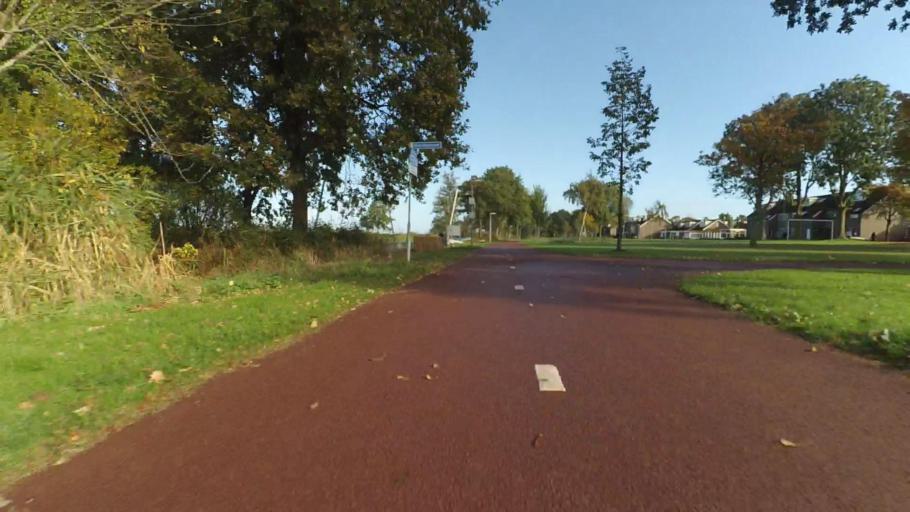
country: NL
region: Gelderland
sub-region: Gemeente Harderwijk
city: Harderwijk
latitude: 52.3367
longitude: 5.5988
